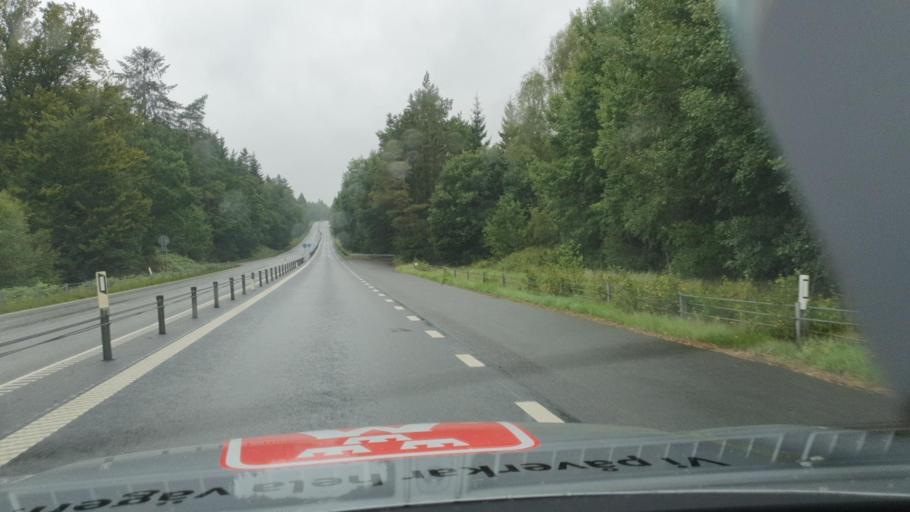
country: SE
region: Skane
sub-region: Ostra Goinge Kommun
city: Broby
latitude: 56.2650
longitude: 14.0451
